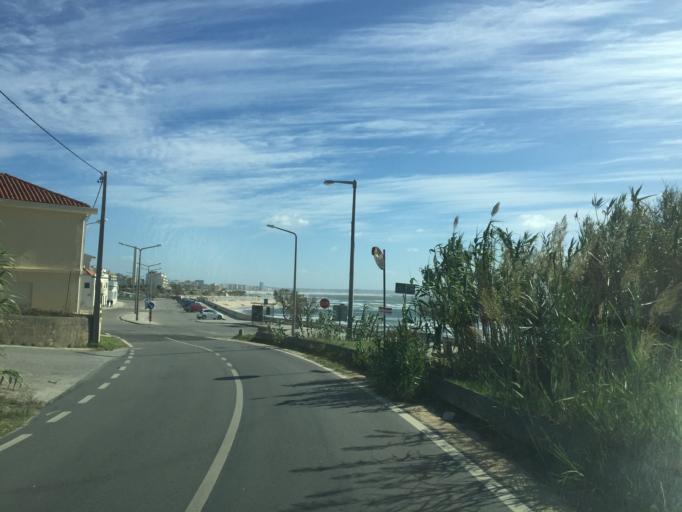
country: PT
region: Coimbra
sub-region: Figueira da Foz
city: Buarcos
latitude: 40.1774
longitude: -8.8998
